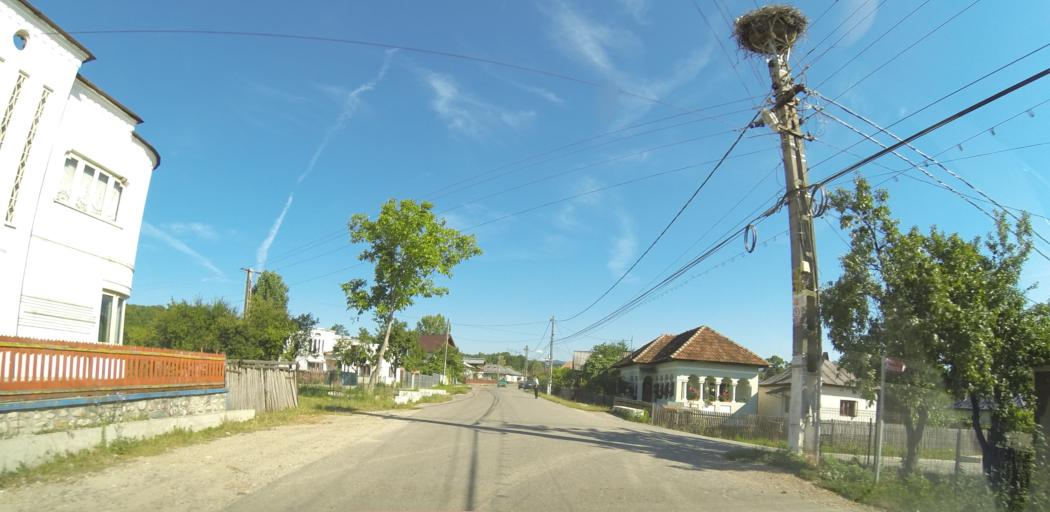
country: RO
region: Valcea
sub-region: Comuna Slatioara
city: Slatioara
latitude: 45.1409
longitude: 23.8713
